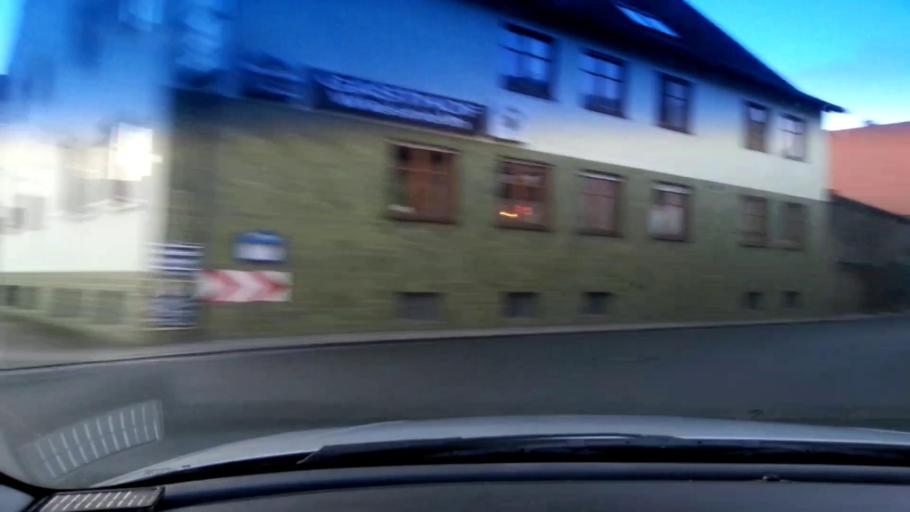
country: DE
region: Bavaria
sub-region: Upper Franconia
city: Pommersfelden
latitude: 49.7794
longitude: 10.8383
